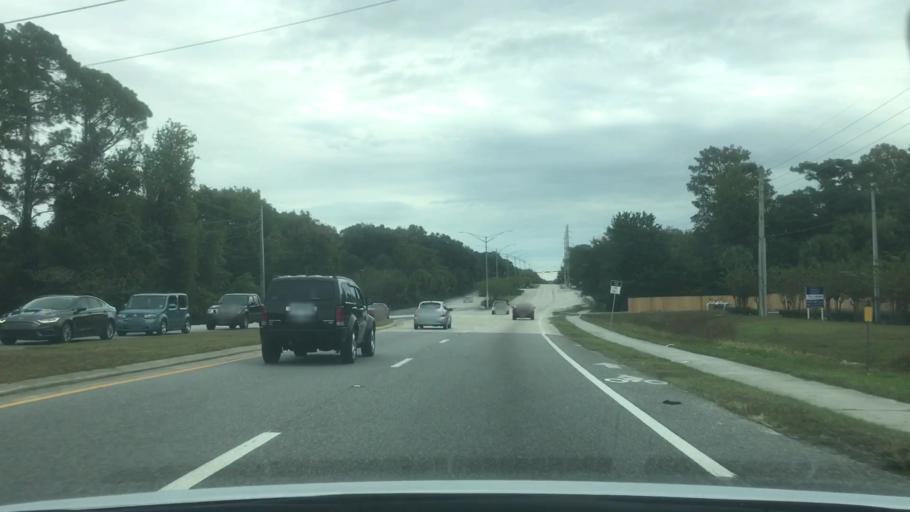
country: US
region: Florida
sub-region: Duval County
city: Jacksonville
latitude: 30.3415
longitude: -81.5404
